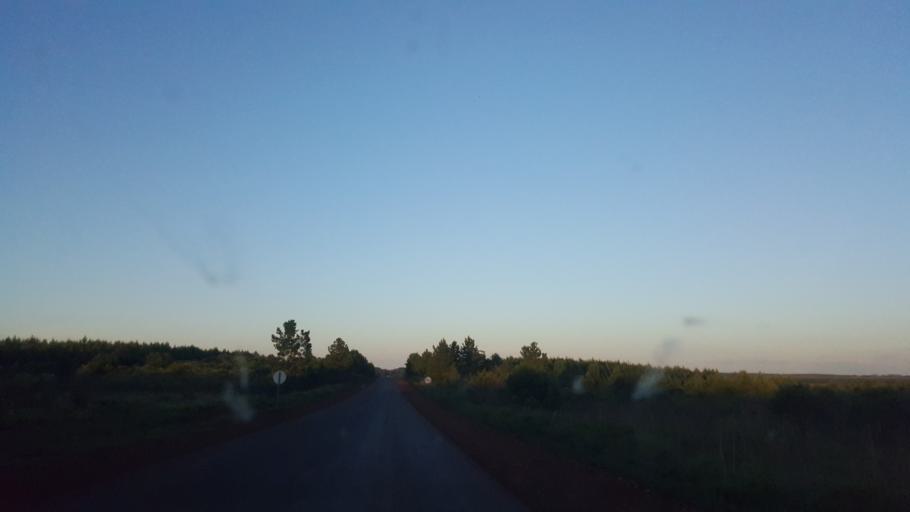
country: AR
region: Corrientes
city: Santo Tome
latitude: -28.3974
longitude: -55.9733
